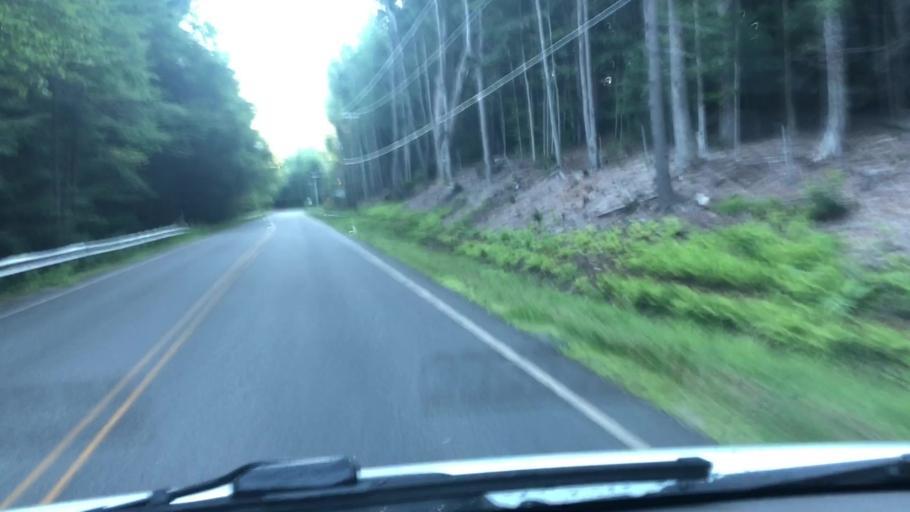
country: US
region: Massachusetts
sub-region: Berkshire County
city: Hinsdale
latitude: 42.4677
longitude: -72.9869
